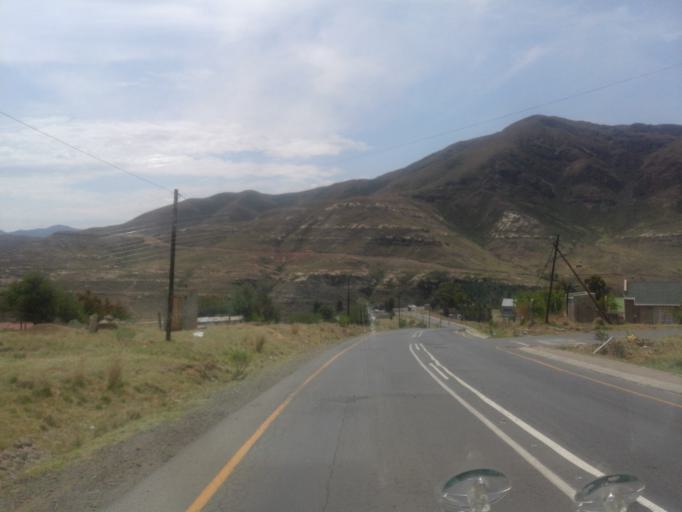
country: LS
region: Qacha's Nek
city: Qacha's Nek
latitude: -30.1073
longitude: 28.6704
